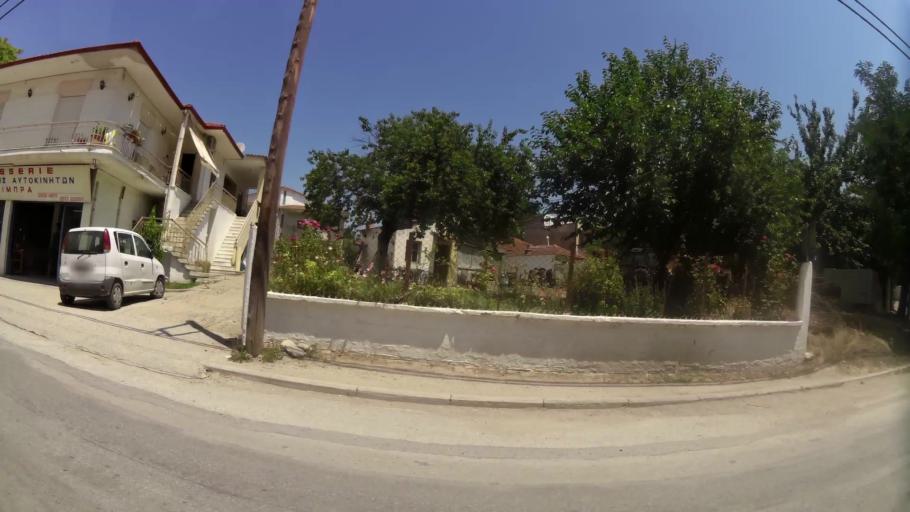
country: GR
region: Central Macedonia
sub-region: Nomos Thessalonikis
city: Epanomi
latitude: 40.4295
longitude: 22.9244
